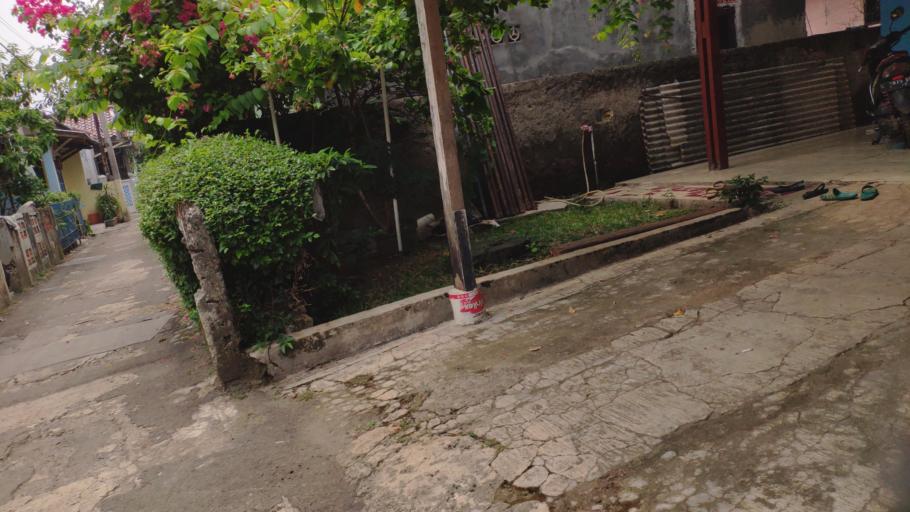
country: ID
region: West Java
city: Depok
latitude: -6.3668
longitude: 106.8070
